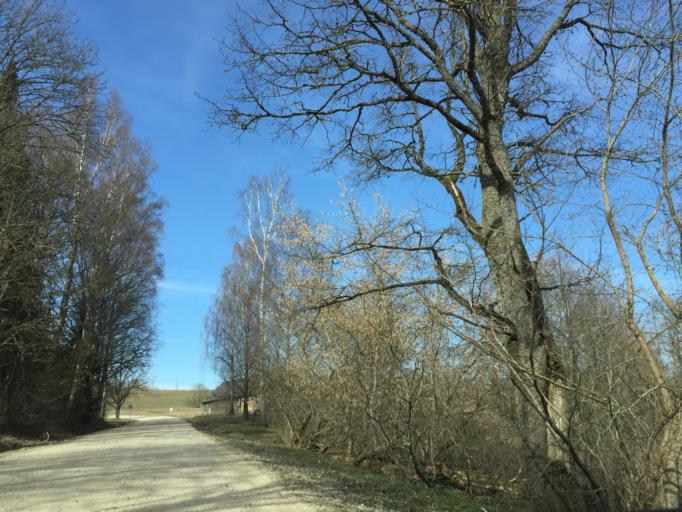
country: EE
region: Vorumaa
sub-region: Antsla vald
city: Vana-Antsla
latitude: 57.9464
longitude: 26.3756
